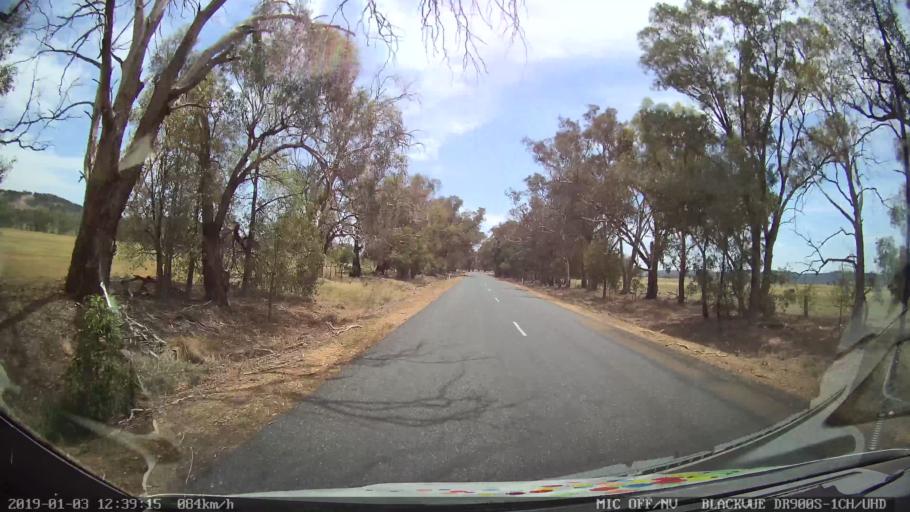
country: AU
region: New South Wales
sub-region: Weddin
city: Grenfell
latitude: -33.8263
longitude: 148.2039
